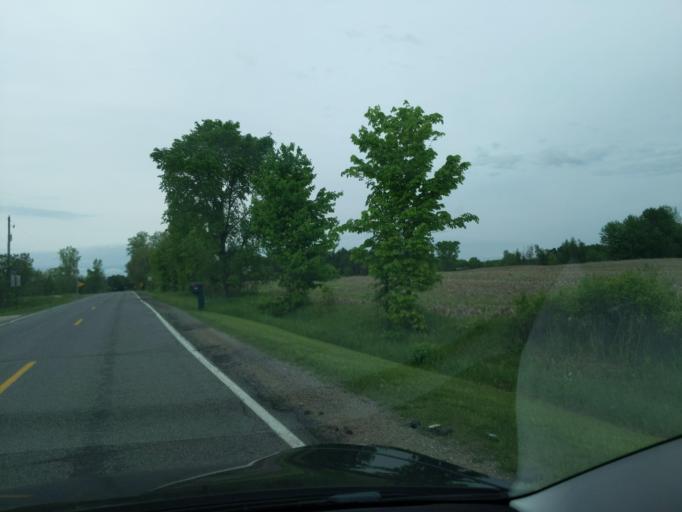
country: US
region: Michigan
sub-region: Ingham County
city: Mason
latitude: 42.5292
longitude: -84.4281
